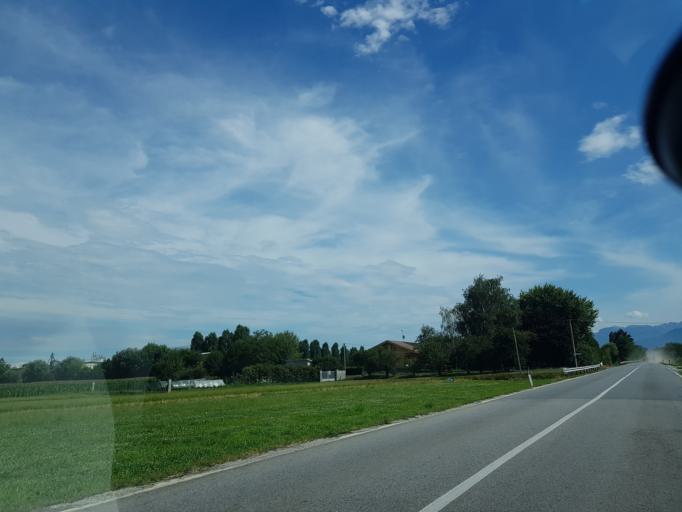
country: IT
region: Piedmont
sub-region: Provincia di Cuneo
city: Roata Rossi
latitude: 44.4592
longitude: 7.5196
